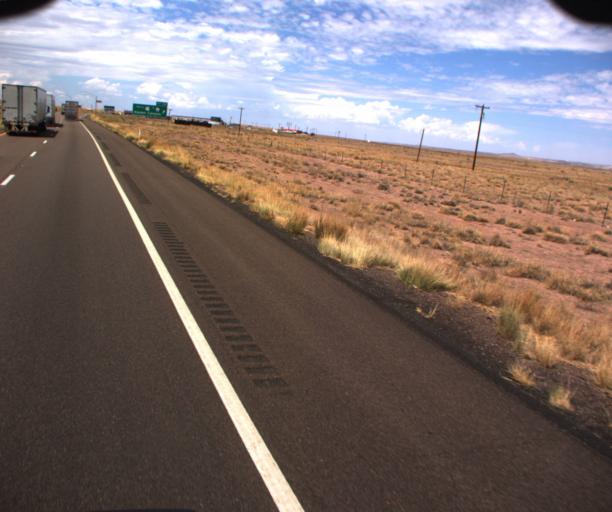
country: US
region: Arizona
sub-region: Navajo County
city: Holbrook
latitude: 34.9761
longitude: -110.0798
